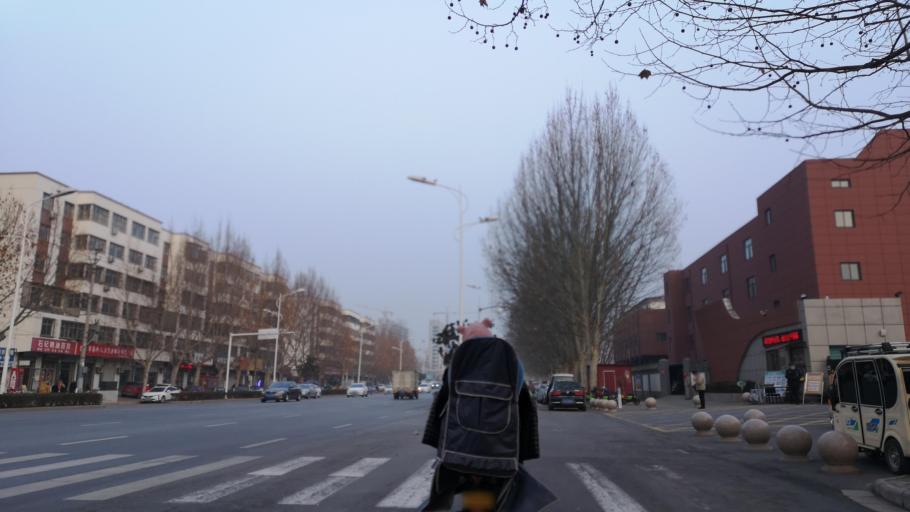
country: CN
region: Henan Sheng
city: Puyang
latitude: 35.7486
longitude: 115.0372
